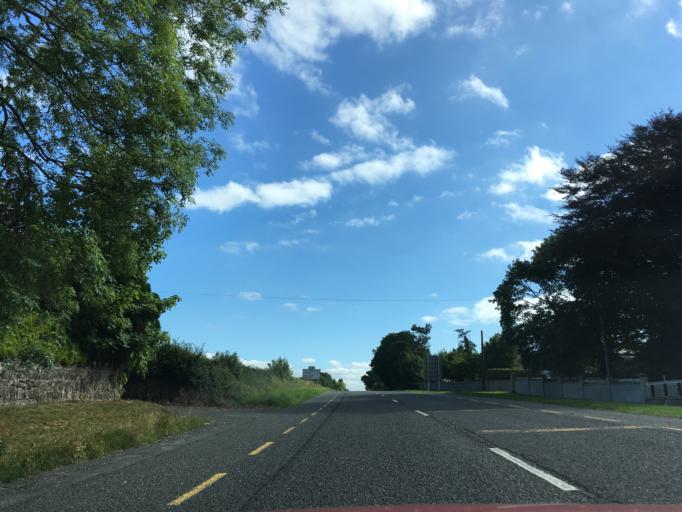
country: IE
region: Munster
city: Cashel
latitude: 52.4947
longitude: -7.8897
